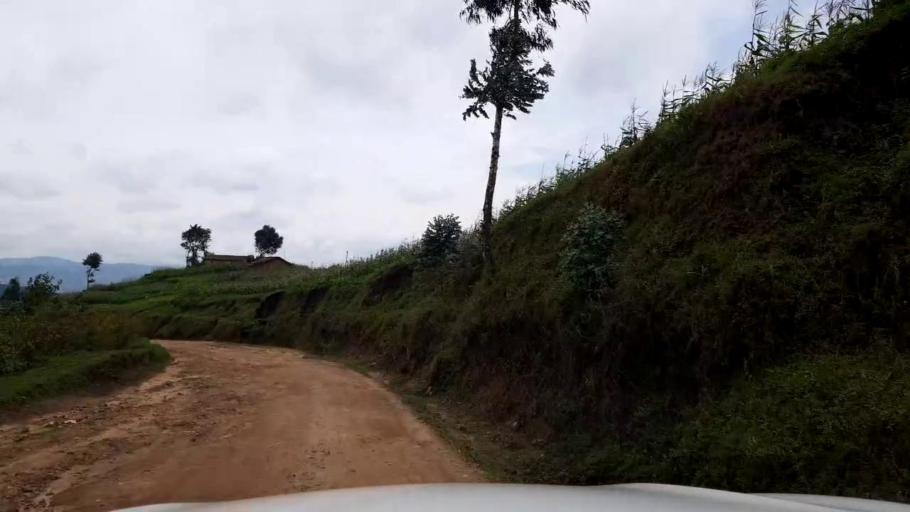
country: RW
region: Western Province
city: Kibuye
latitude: -1.9540
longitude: 29.4194
